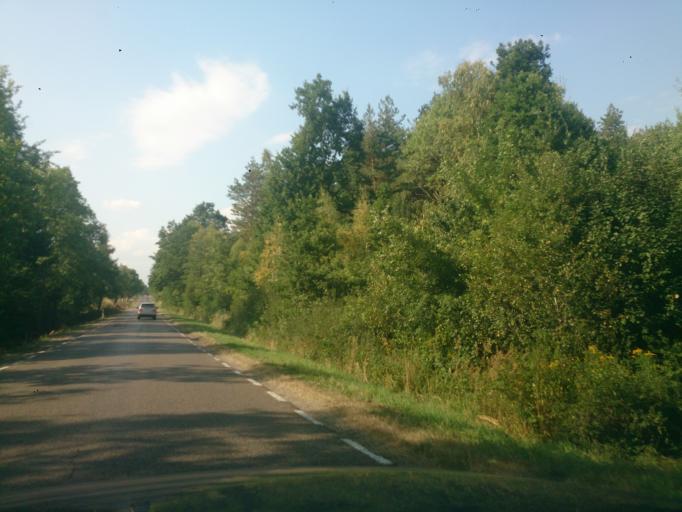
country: PL
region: Swietokrzyskie
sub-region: Powiat opatowski
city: Iwaniska
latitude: 50.7004
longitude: 21.3320
